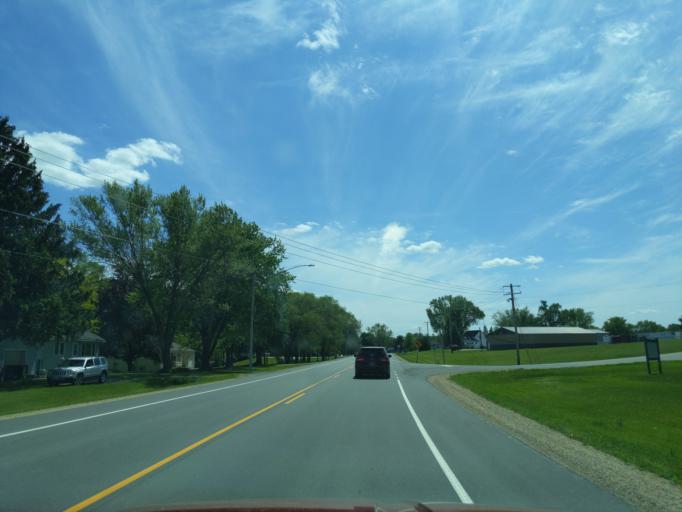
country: US
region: Wisconsin
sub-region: Columbia County
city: Pardeeville
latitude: 43.5005
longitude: -89.3065
